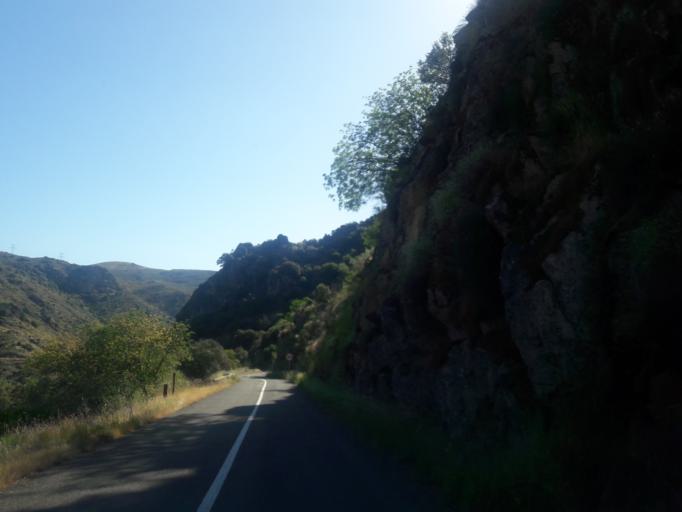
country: ES
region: Castille and Leon
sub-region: Provincia de Salamanca
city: Saucelle
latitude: 41.0235
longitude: -6.7436
